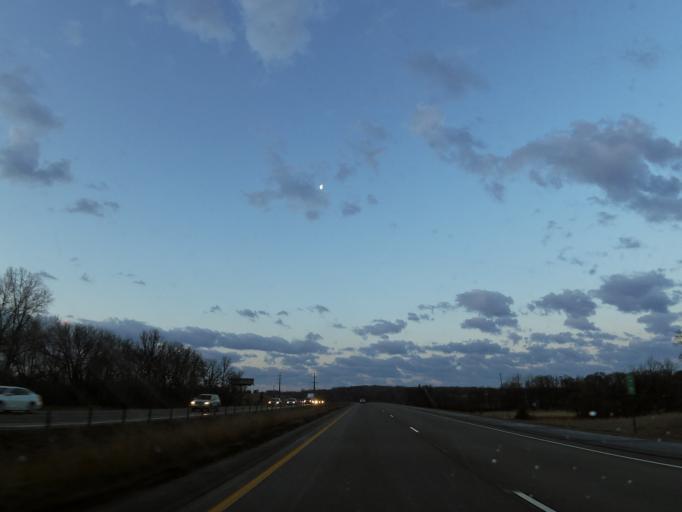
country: US
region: Minnesota
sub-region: Scott County
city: Elko New Market
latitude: 44.6047
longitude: -93.2970
